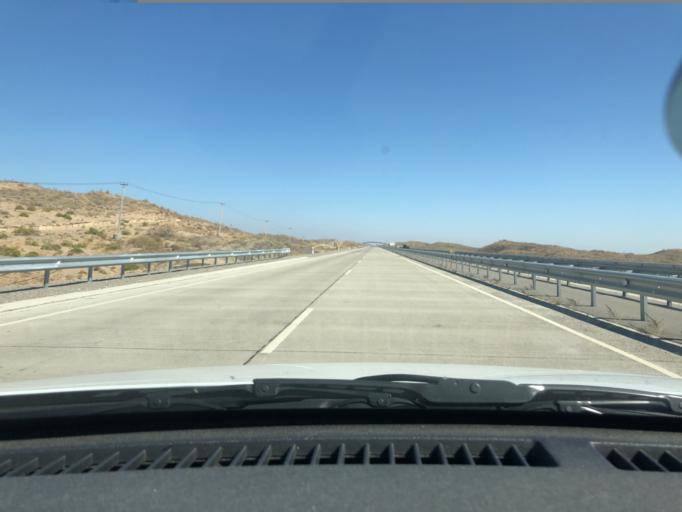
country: KZ
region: Almaty Oblysy
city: Zharkent
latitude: 44.1748
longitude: 80.2940
